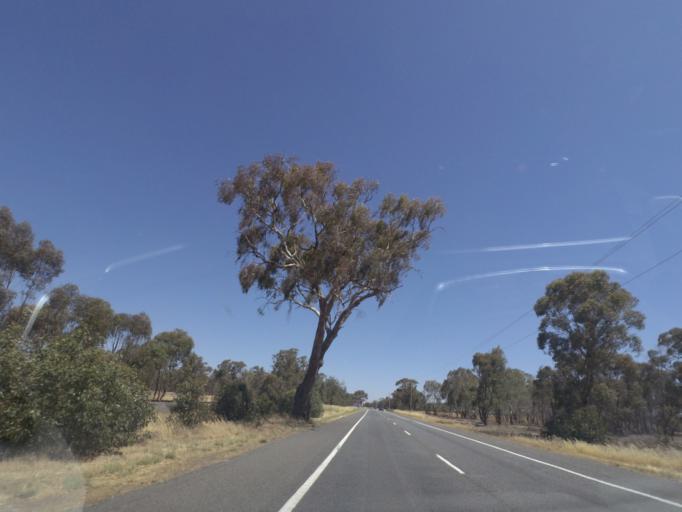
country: AU
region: Victoria
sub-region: Greater Shepparton
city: Shepparton
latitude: -36.2256
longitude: 145.4318
